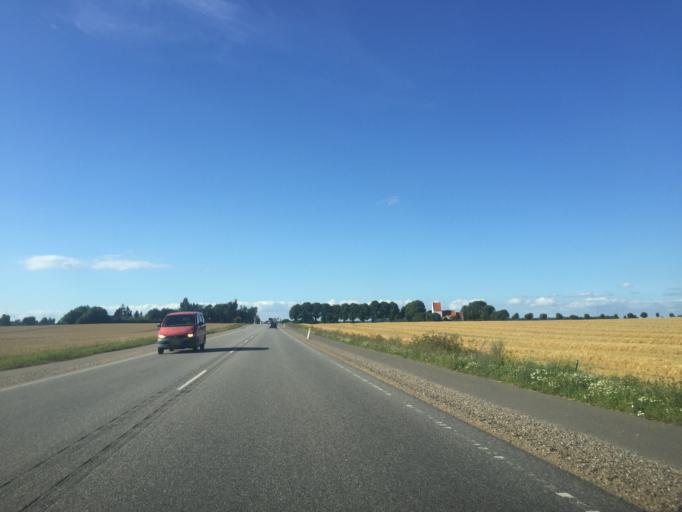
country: DK
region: Zealand
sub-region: Guldborgsund Kommune
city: Norre Alslev
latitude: 54.8437
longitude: 11.8585
